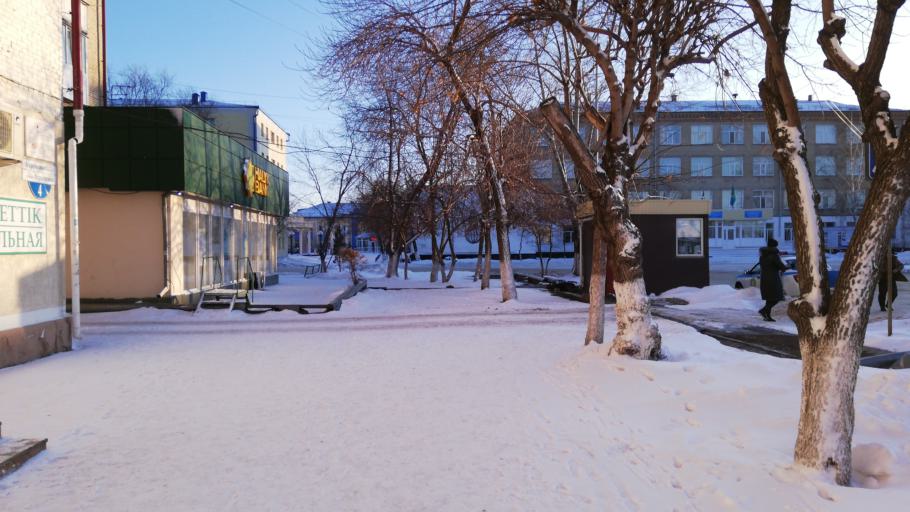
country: KZ
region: Soltustik Qazaqstan
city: Petropavlovsk
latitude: 54.8579
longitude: 69.1708
